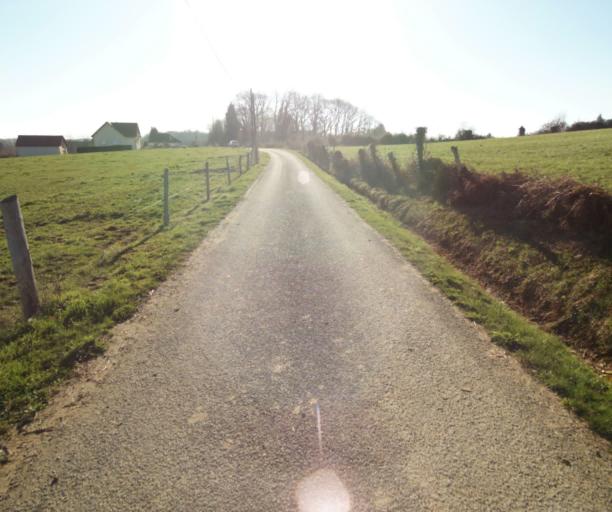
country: FR
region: Limousin
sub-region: Departement de la Correze
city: Saint-Clement
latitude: 45.3904
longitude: 1.6366
